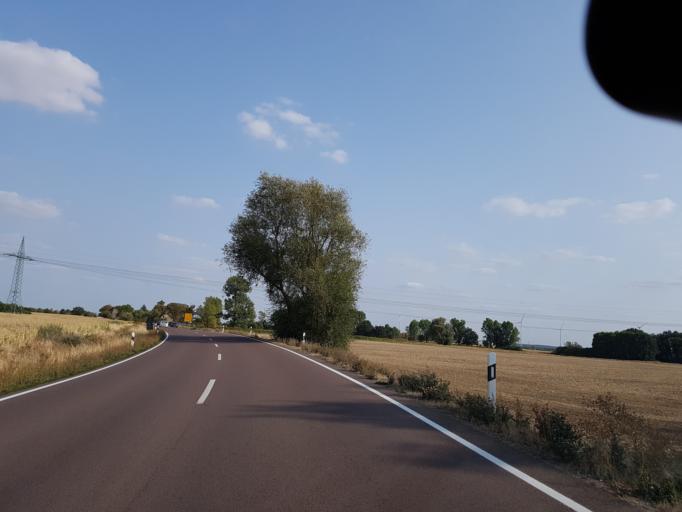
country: DE
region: Saxony-Anhalt
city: Kemberg
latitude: 51.8095
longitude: 12.6445
